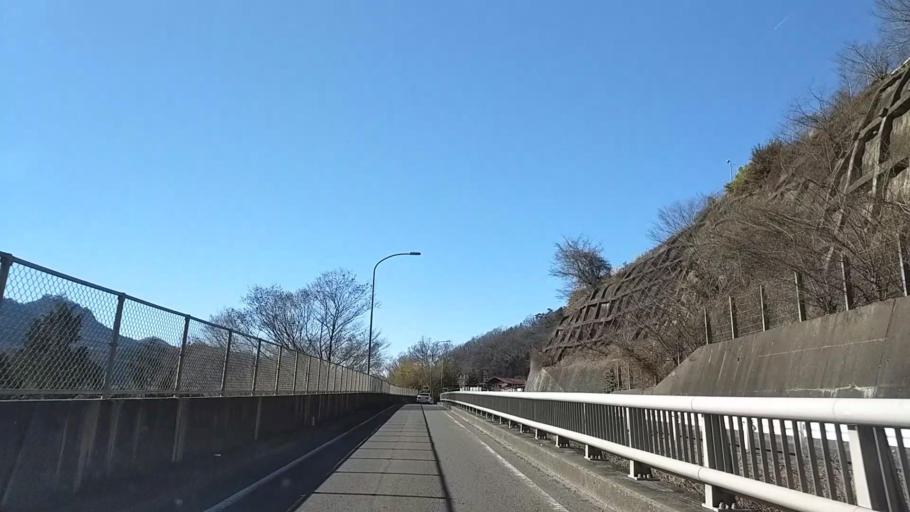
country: JP
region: Yamanashi
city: Otsuki
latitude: 35.6175
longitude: 138.9893
